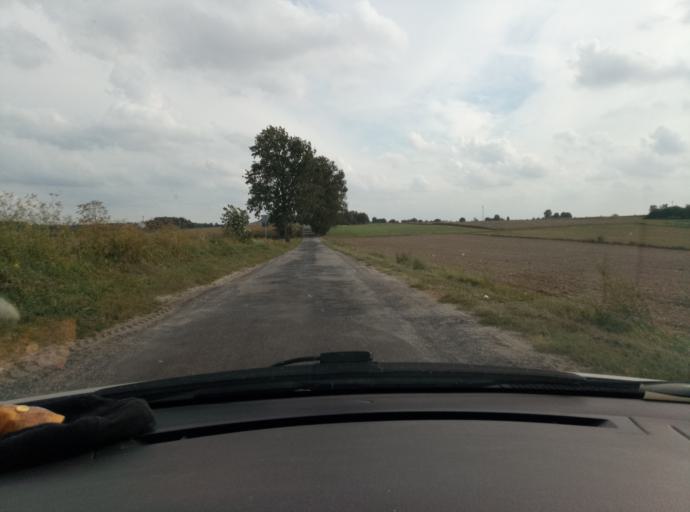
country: PL
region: Kujawsko-Pomorskie
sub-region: Powiat brodnicki
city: Jablonowo Pomorskie
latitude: 53.3841
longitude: 19.2456
